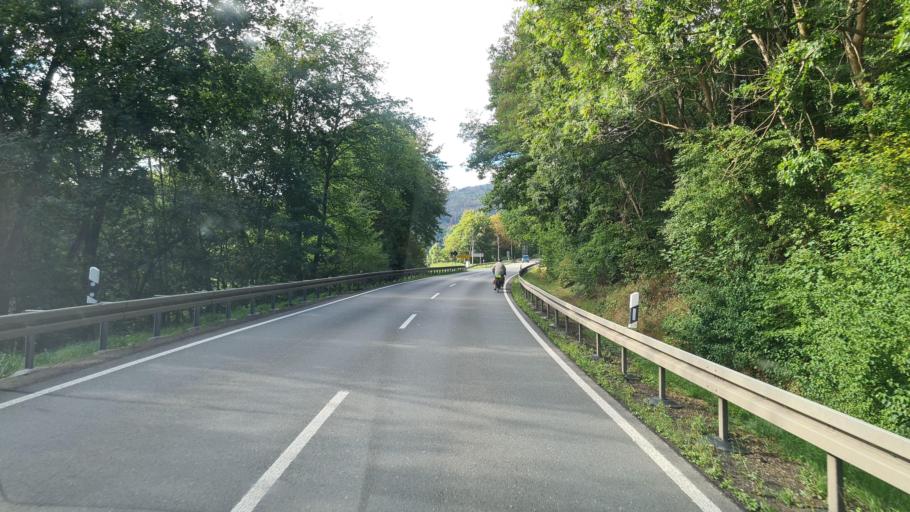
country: DE
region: Thuringia
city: Saalfeld
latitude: 50.6163
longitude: 11.3938
